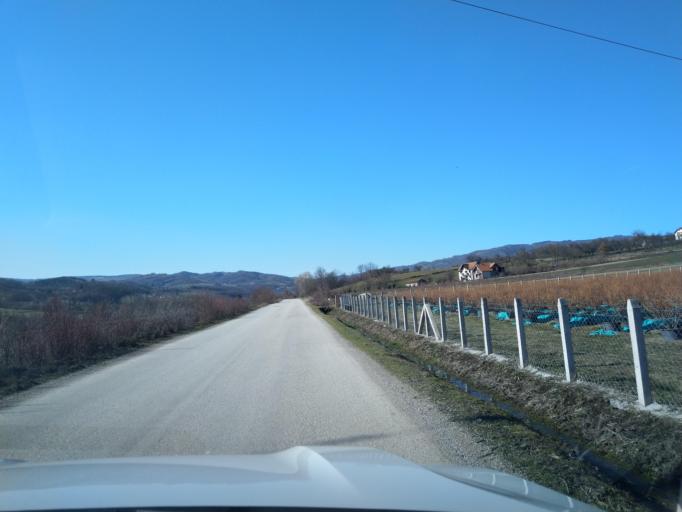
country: RS
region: Central Serbia
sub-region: Zlatiborski Okrug
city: Kosjeric
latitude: 43.9300
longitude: 19.8961
